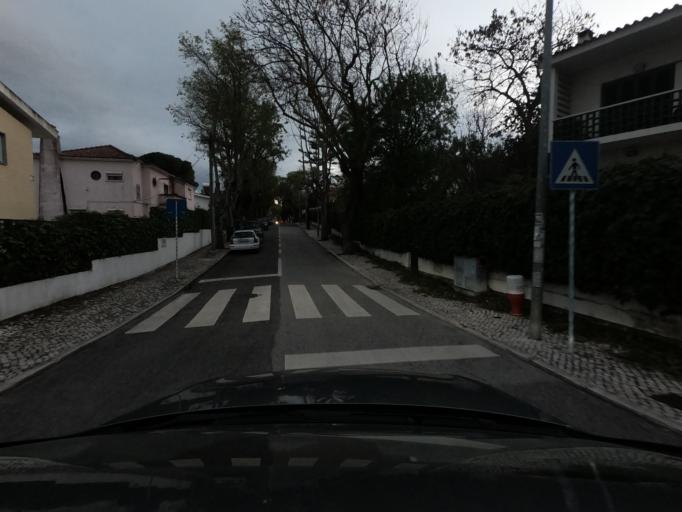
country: PT
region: Lisbon
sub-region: Oeiras
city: Terrugem
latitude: 38.7023
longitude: -9.2771
